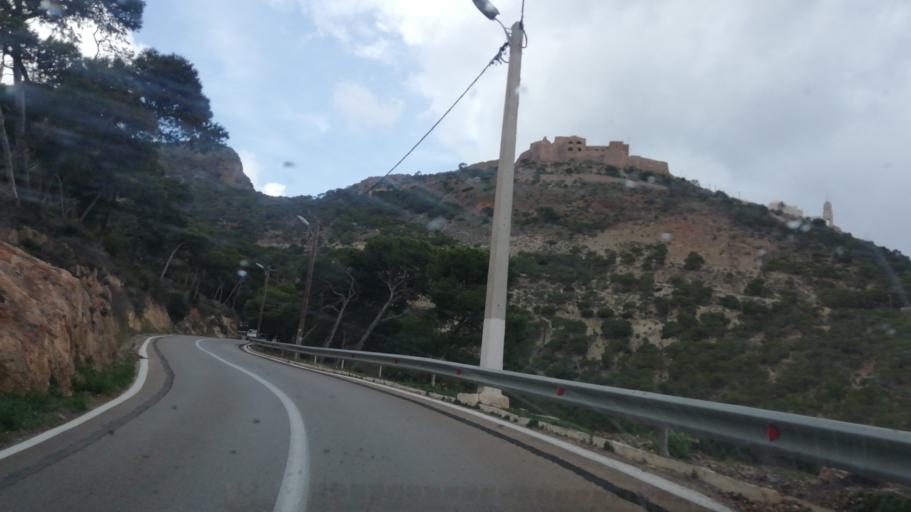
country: DZ
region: Oran
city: Oran
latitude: 35.7045
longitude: -0.6622
